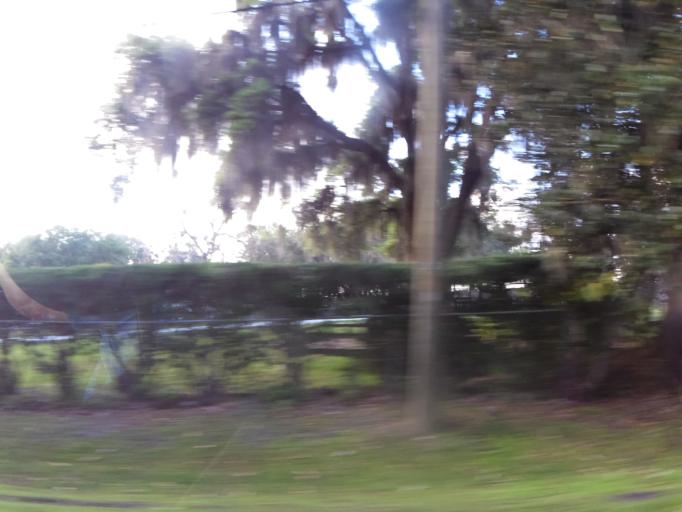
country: US
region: Florida
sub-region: Saint Johns County
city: Fruit Cove
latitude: 30.1294
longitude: -81.6193
